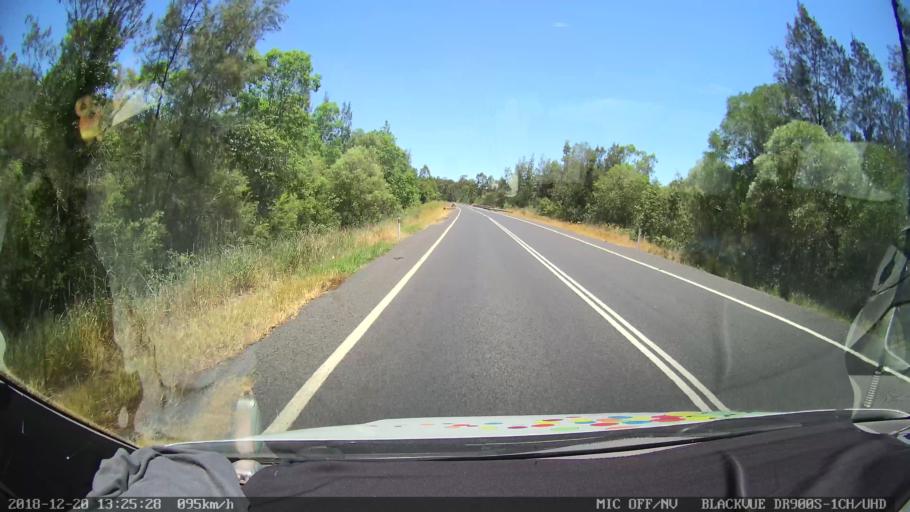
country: AU
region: New South Wales
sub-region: Richmond Valley
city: Casino
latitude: -29.1316
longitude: 152.9963
